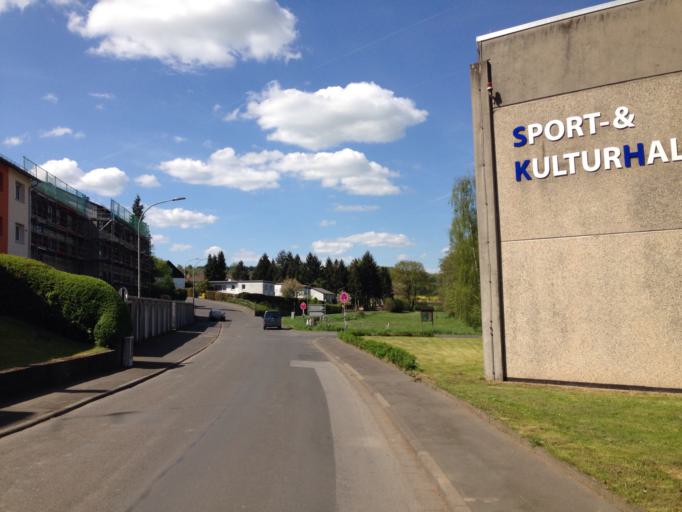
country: DE
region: Hesse
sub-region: Regierungsbezirk Giessen
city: Laubach
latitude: 50.5487
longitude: 8.9873
